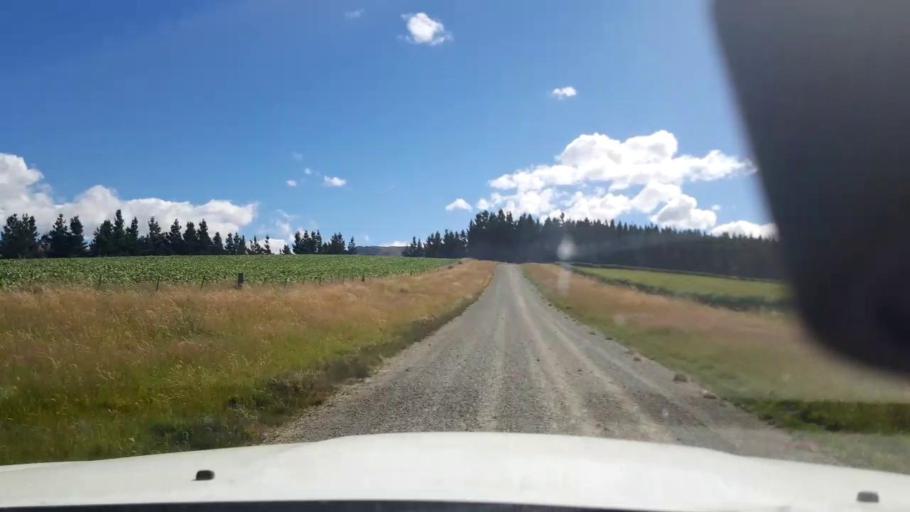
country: NZ
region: Canterbury
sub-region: Timaru District
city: Pleasant Point
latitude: -44.3202
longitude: 170.8813
